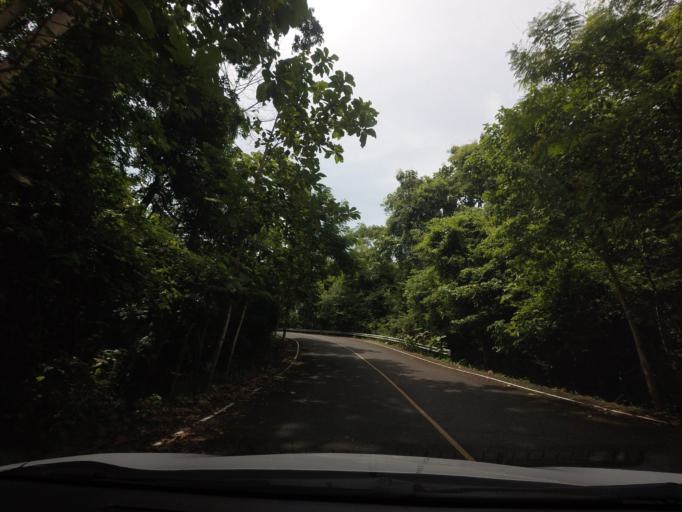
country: TH
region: Chon Buri
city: Ban Bueng
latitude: 13.2121
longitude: 101.0707
